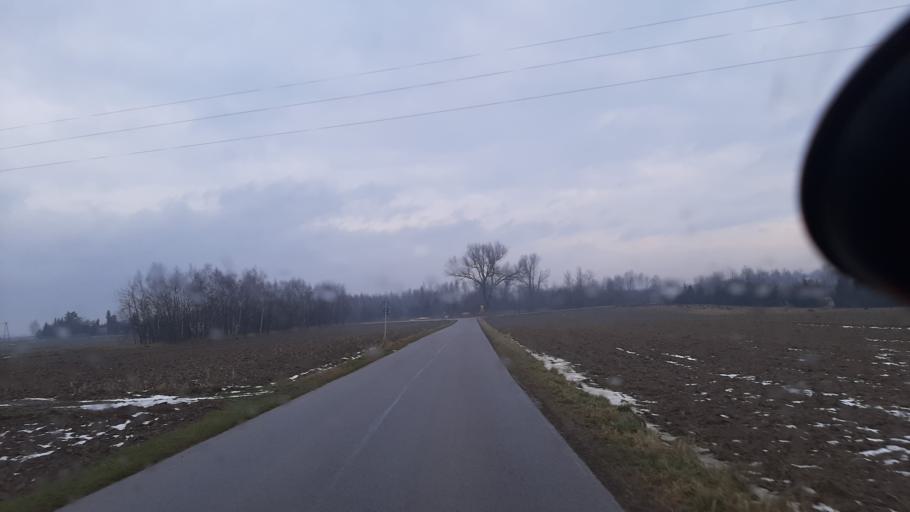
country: PL
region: Lublin Voivodeship
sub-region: Powiat lubelski
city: Niemce
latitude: 51.3357
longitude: 22.5859
